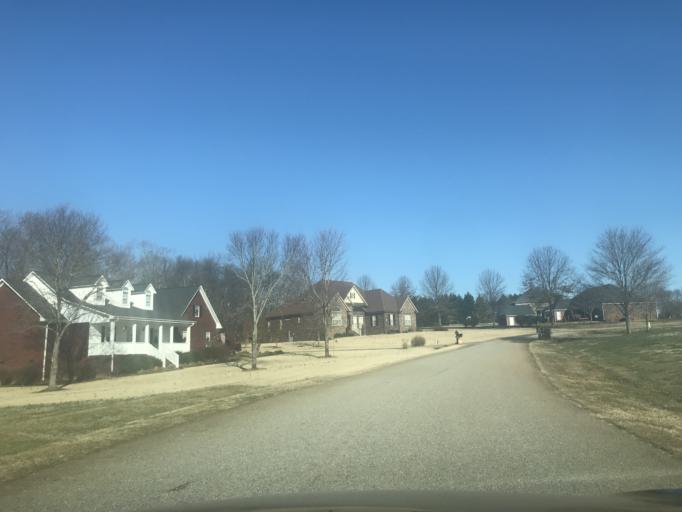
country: US
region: South Carolina
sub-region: Cherokee County
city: Gaffney
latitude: 35.1220
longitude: -81.6925
